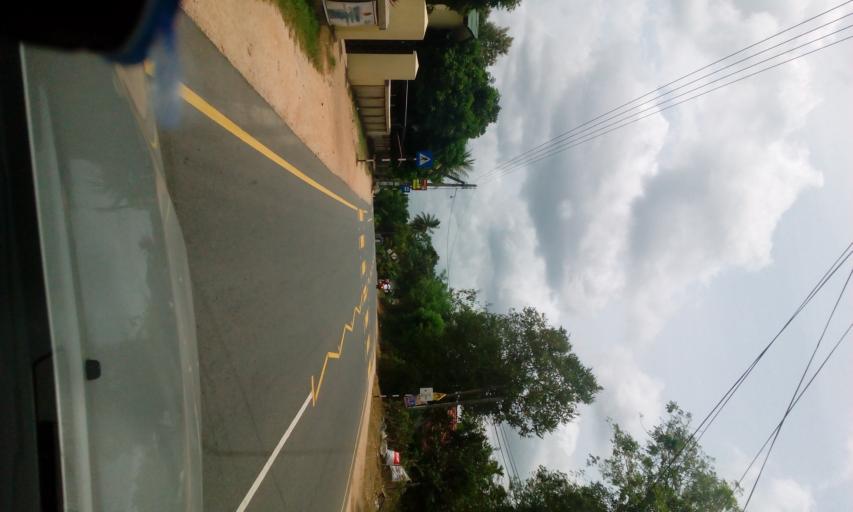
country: LK
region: North Western
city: Kuliyapitiya
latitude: 7.4558
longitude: 80.1420
